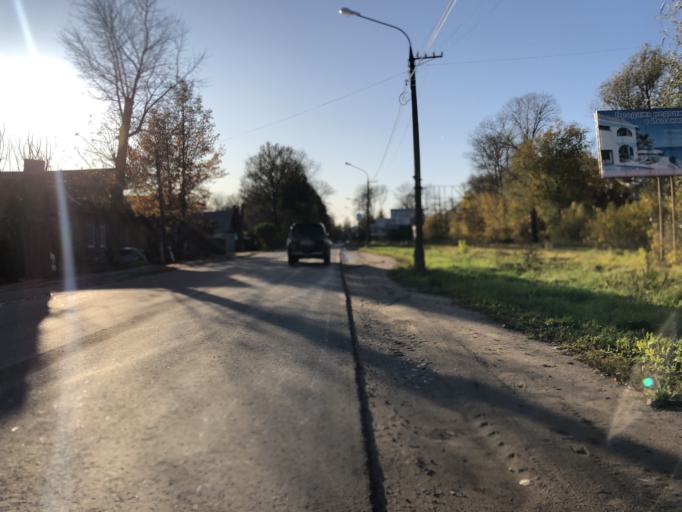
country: RU
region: Tverskaya
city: Rzhev
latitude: 56.2465
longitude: 34.3343
